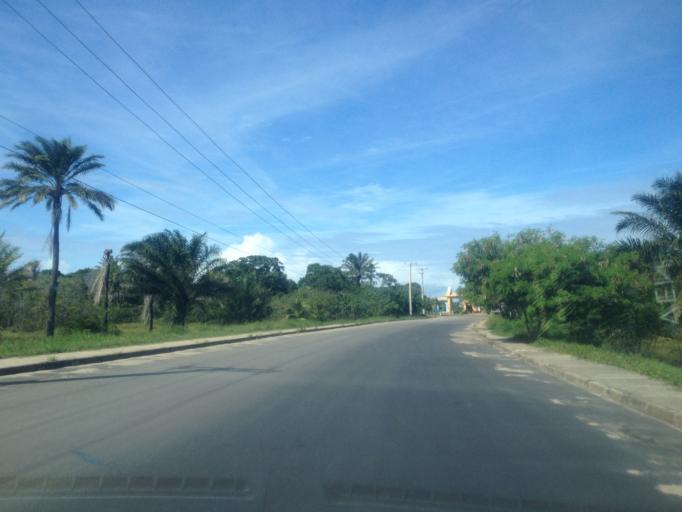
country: BR
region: Bahia
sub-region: Mata De Sao Joao
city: Mata de Sao Joao
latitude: -12.5419
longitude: -37.9932
